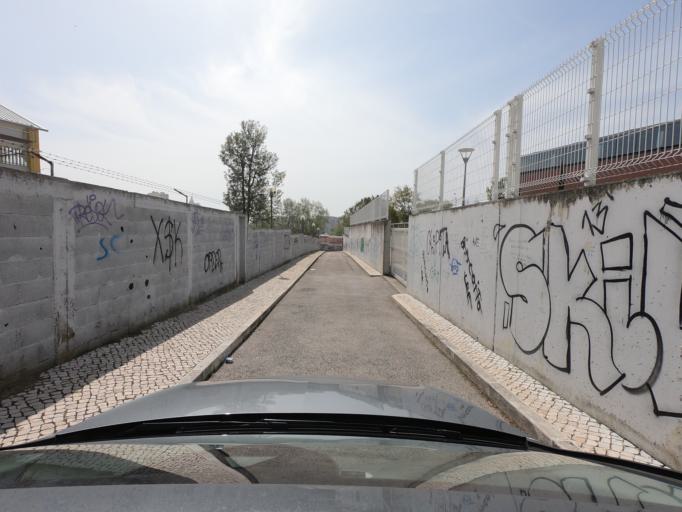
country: PT
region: Lisbon
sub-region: Loures
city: Moscavide
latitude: 38.7707
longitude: -9.1071
